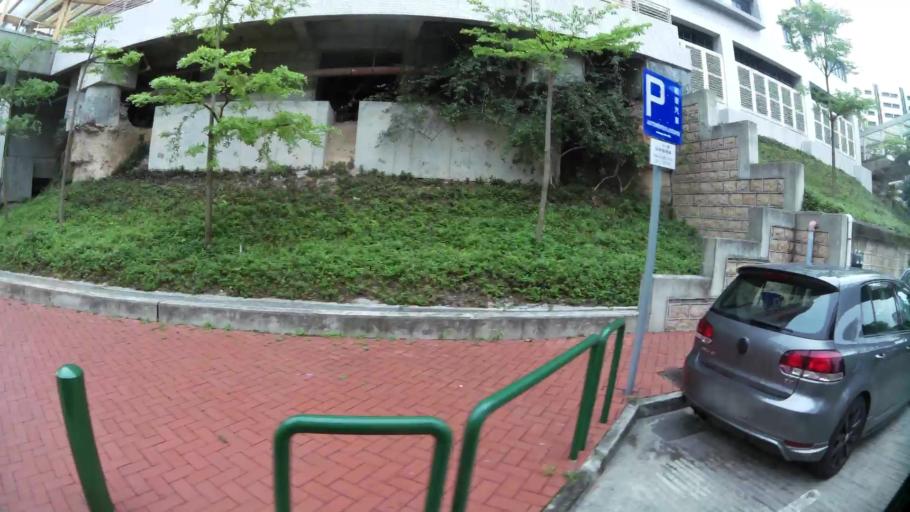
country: MO
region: Macau
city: Macau
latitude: 22.1639
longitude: 113.5597
